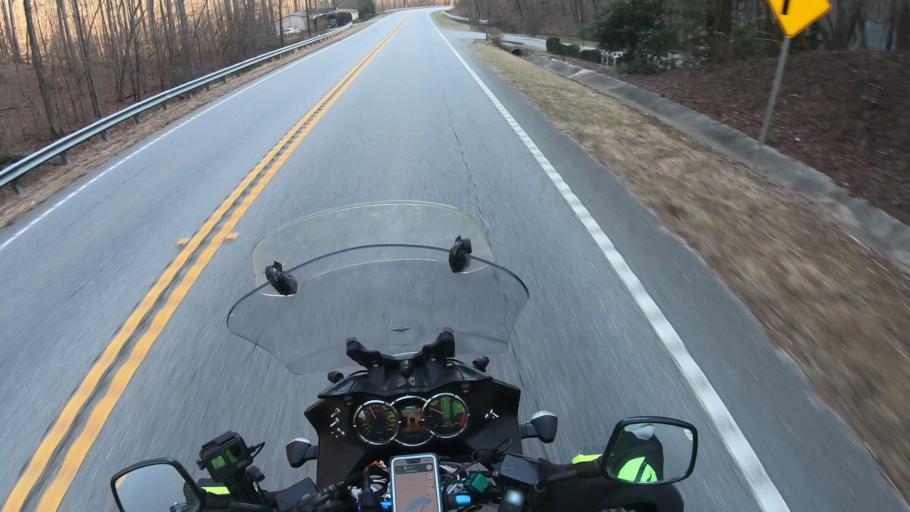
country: US
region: Georgia
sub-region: Lumpkin County
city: Dahlonega
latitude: 34.5525
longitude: -83.9719
